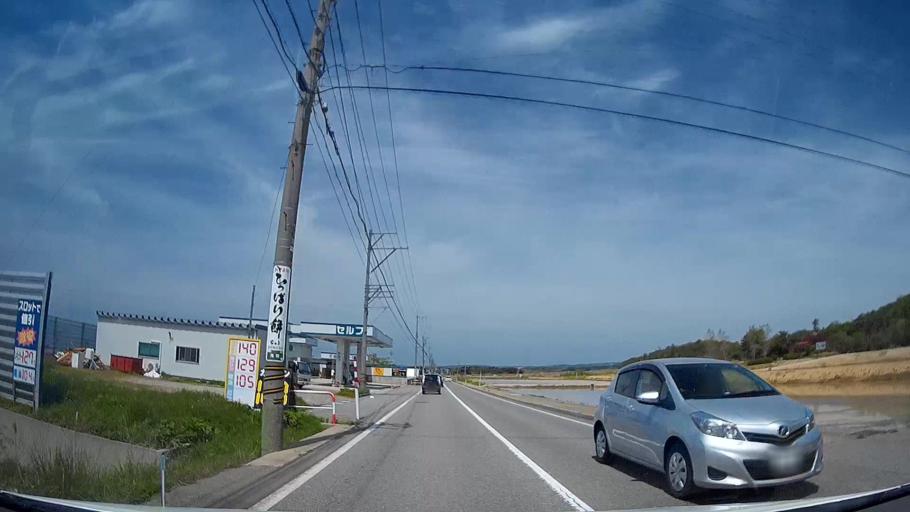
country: JP
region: Ishikawa
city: Hakui
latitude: 36.9360
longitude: 136.7582
